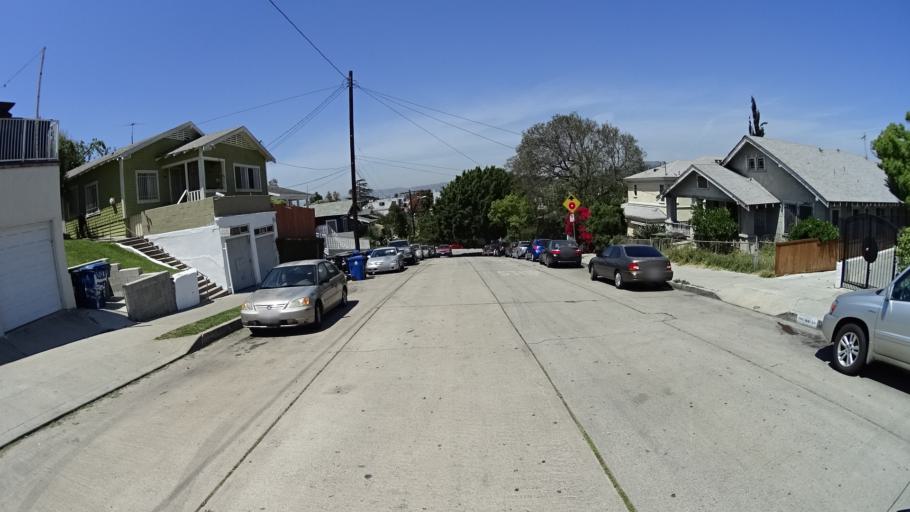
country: US
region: California
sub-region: Los Angeles County
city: Echo Park
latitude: 34.0747
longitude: -118.2553
